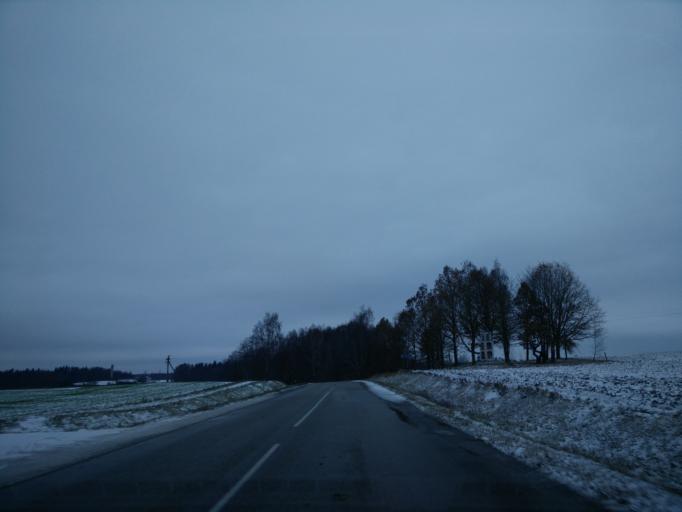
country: LT
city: Tytuveneliai
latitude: 55.5167
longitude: 23.2758
